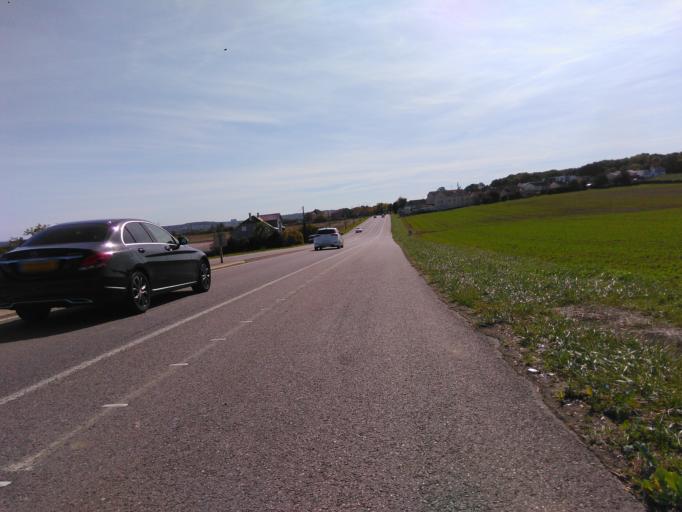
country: FR
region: Lorraine
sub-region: Departement de la Moselle
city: Thionville
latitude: 49.3892
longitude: 6.1686
